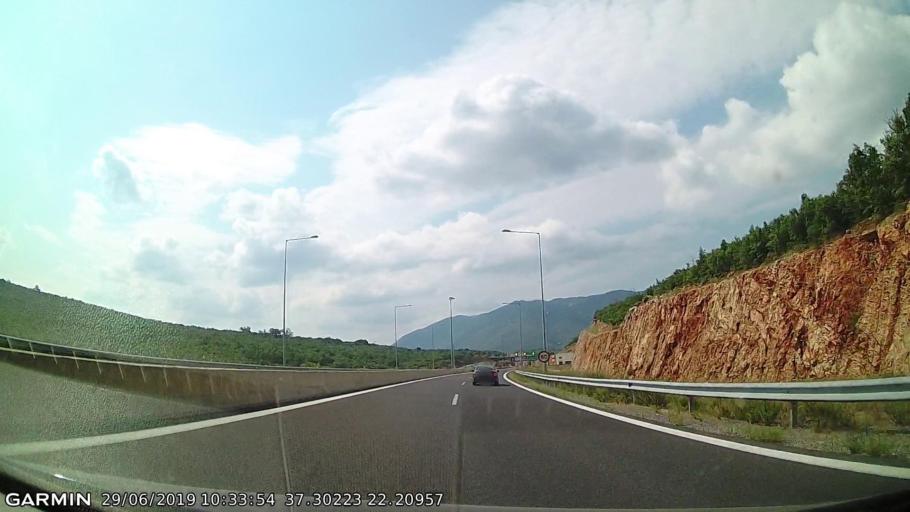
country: GR
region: Peloponnese
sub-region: Nomos Arkadias
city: Megalopoli
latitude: 37.3020
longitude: 22.2095
